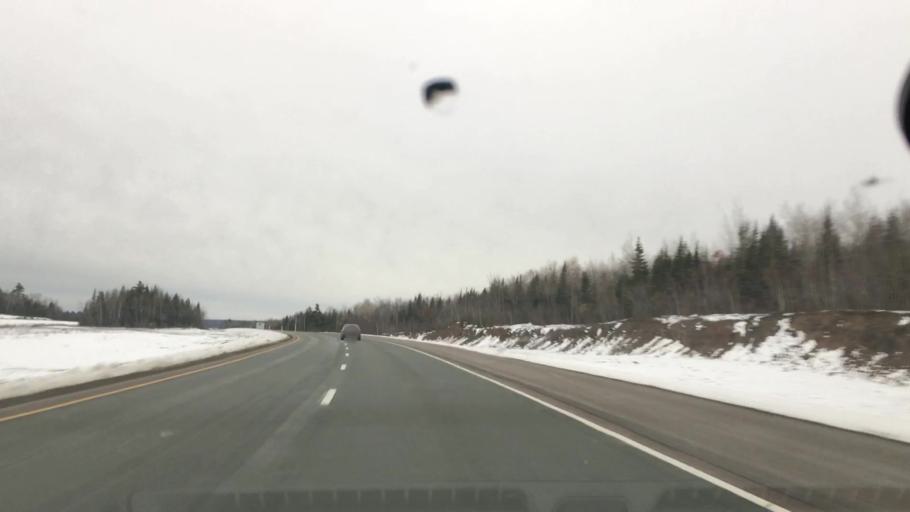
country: CA
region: New Brunswick
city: Fredericton
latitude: 45.9277
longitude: -66.7658
